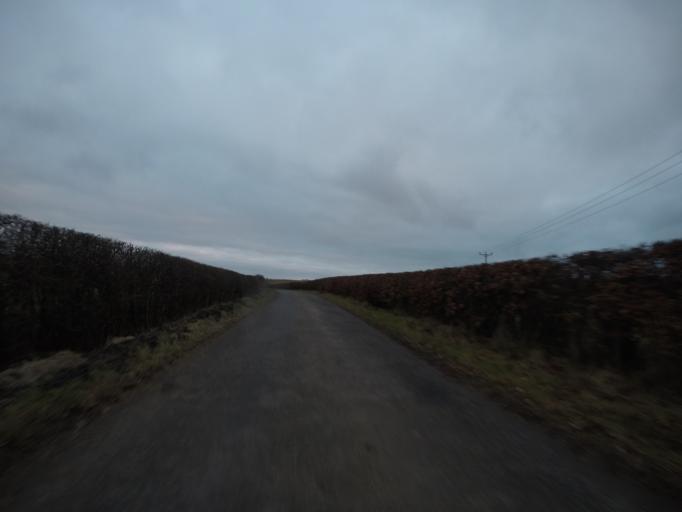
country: GB
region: Scotland
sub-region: North Ayrshire
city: Dalry
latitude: 55.6880
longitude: -4.7424
